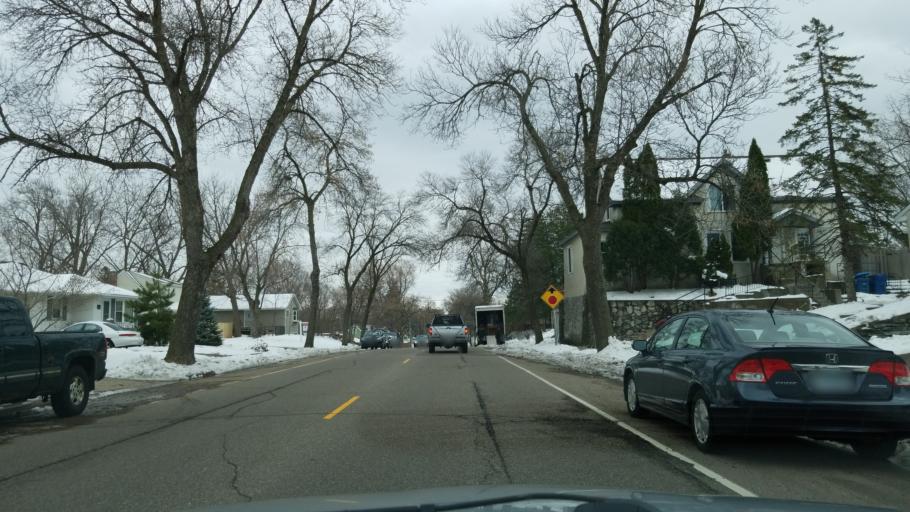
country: US
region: Minnesota
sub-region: Dakota County
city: West Saint Paul
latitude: 44.9124
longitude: -93.0776
